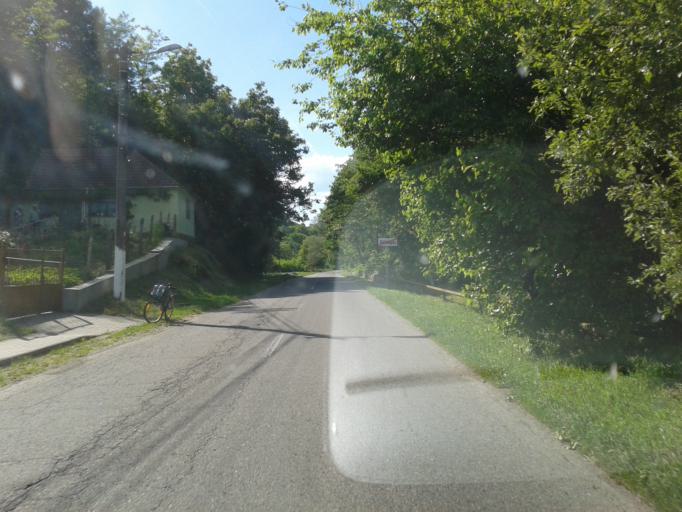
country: RO
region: Hunedoara
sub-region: Comuna Geoagiu
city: Geoagiu
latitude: 45.9349
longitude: 23.1915
